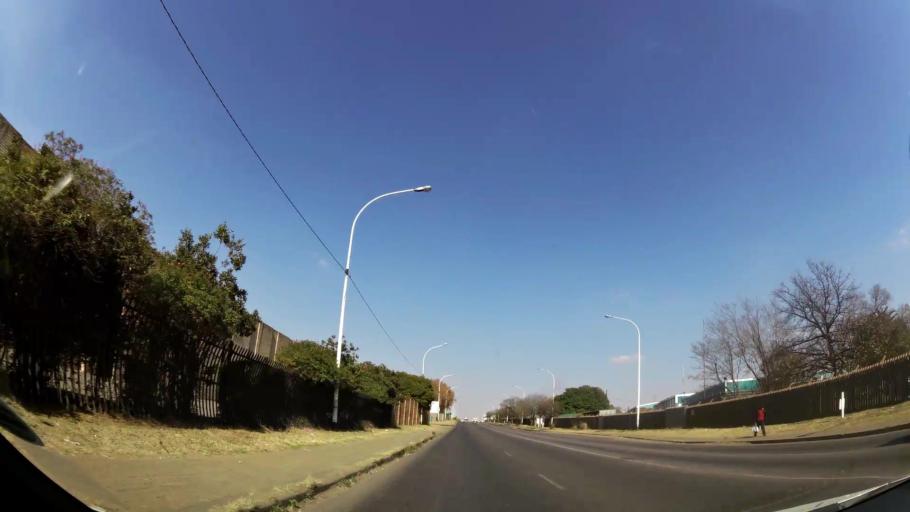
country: ZA
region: Gauteng
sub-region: Ekurhuleni Metropolitan Municipality
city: Boksburg
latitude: -26.2193
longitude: 28.2894
